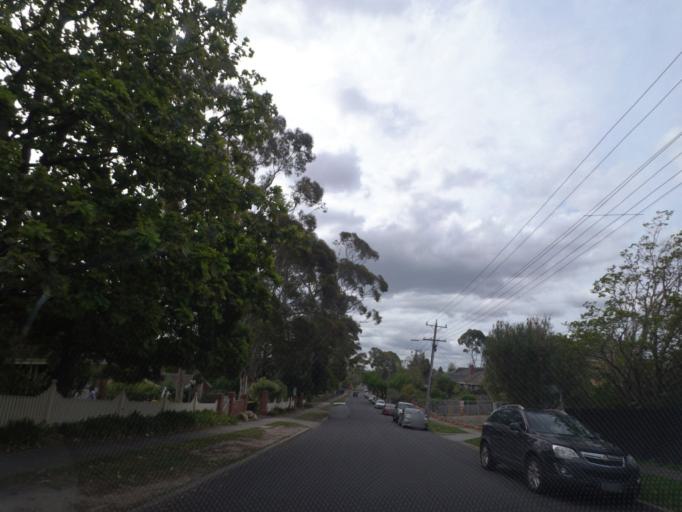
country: AU
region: Victoria
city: Mont Albert
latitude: -37.8059
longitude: 145.0967
